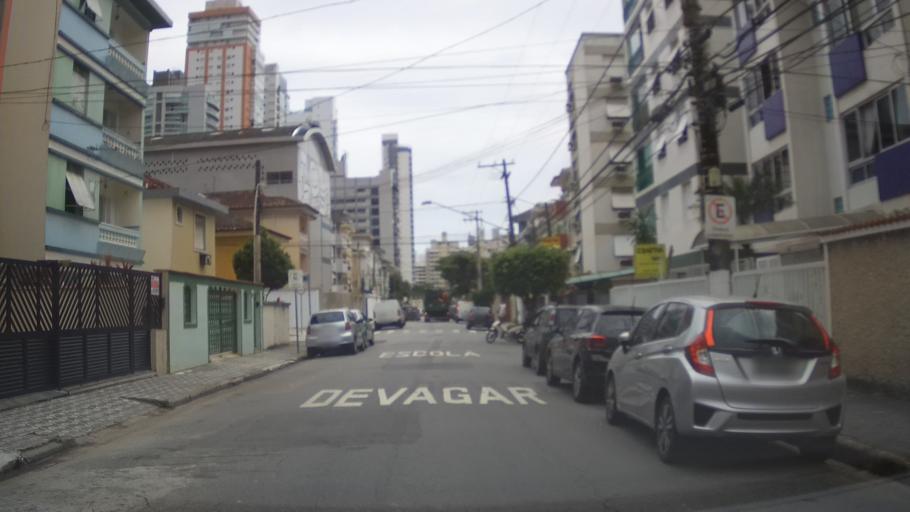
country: BR
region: Sao Paulo
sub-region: Santos
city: Santos
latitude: -23.9678
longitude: -46.3175
